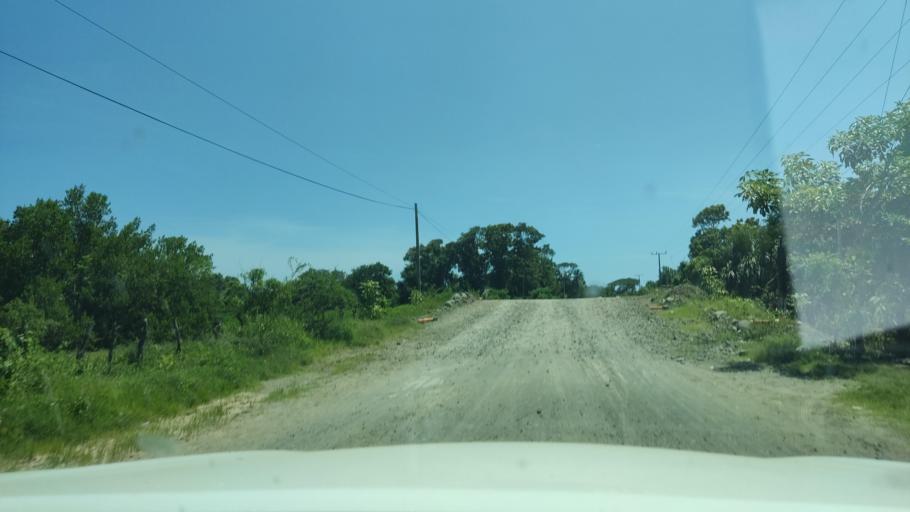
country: SV
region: Ahuachapan
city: San Francisco Menendez
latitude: 13.7652
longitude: -90.1625
